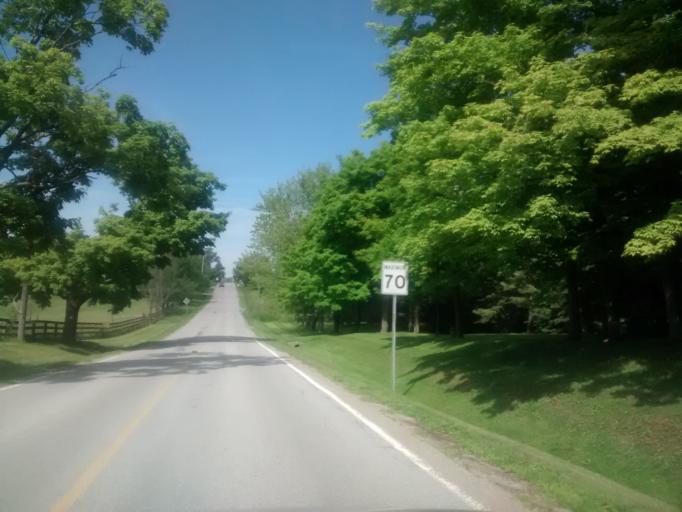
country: CA
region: Ontario
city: Burlington
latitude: 43.4276
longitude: -79.8345
